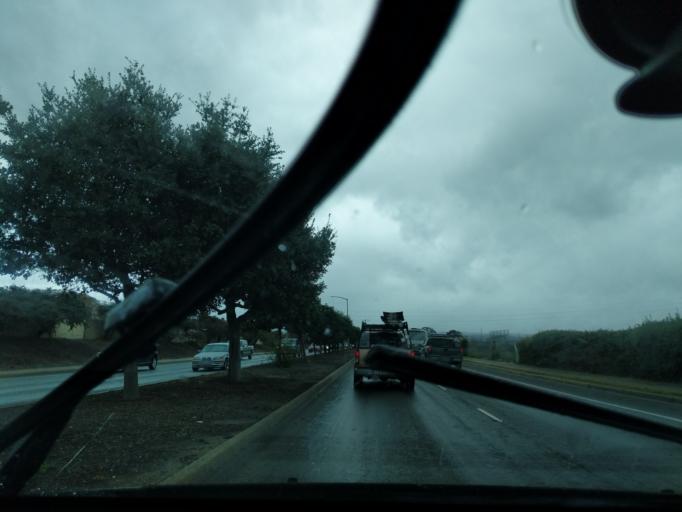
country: US
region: California
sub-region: Monterey County
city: Boronda
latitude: 36.6923
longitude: -121.6691
